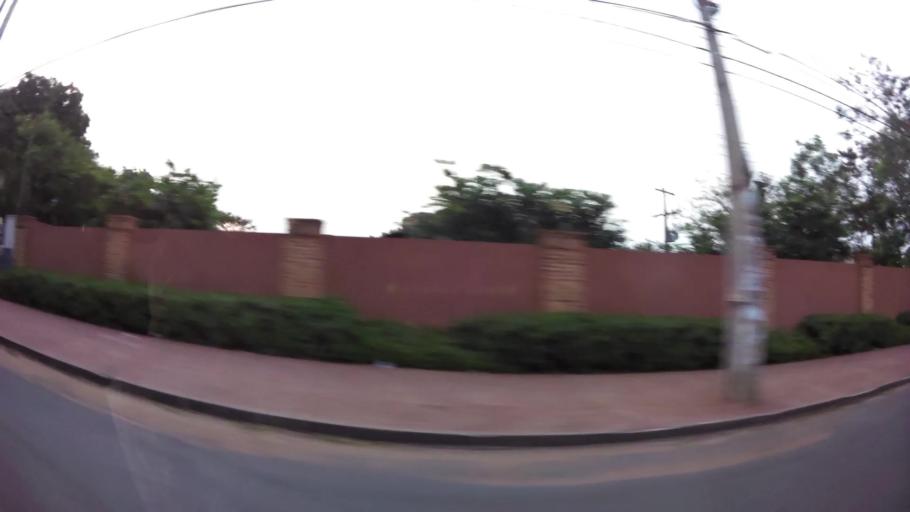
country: PY
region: Central
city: Lambare
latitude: -25.3282
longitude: -57.6184
